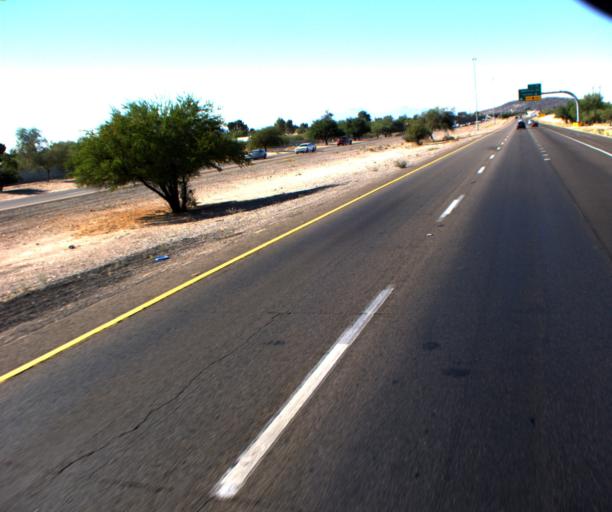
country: US
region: Arizona
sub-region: Pima County
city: Drexel Heights
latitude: 32.1463
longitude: -110.9868
